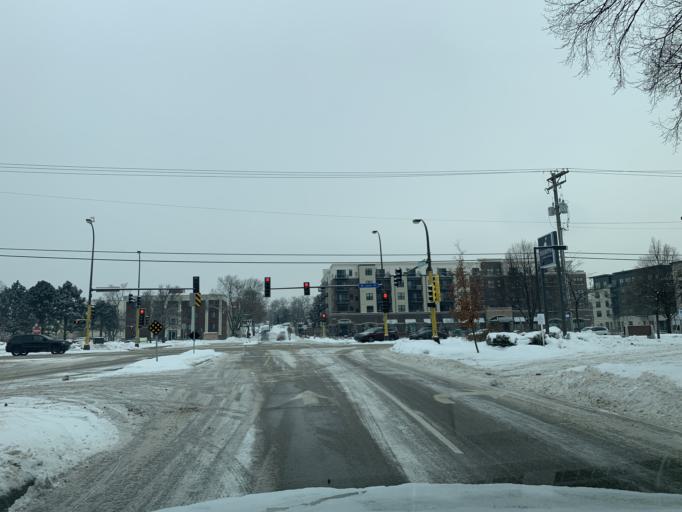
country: US
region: Minnesota
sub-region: Hennepin County
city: Saint Louis Park
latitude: 44.9489
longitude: -93.3289
